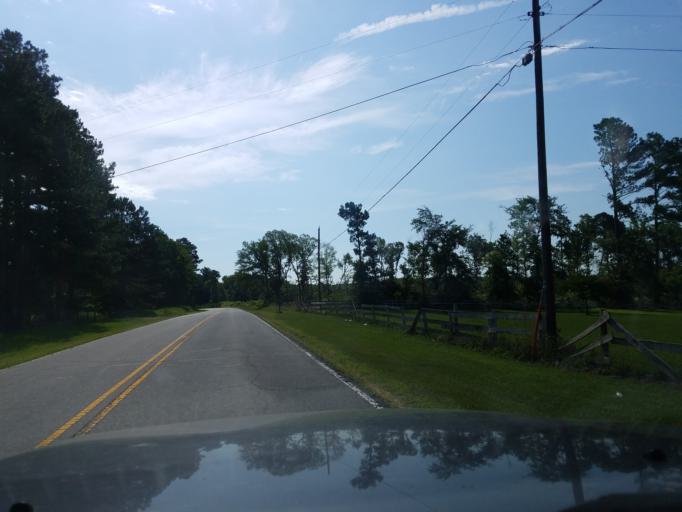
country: US
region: North Carolina
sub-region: Granville County
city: Oxford
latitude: 36.3147
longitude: -78.5267
